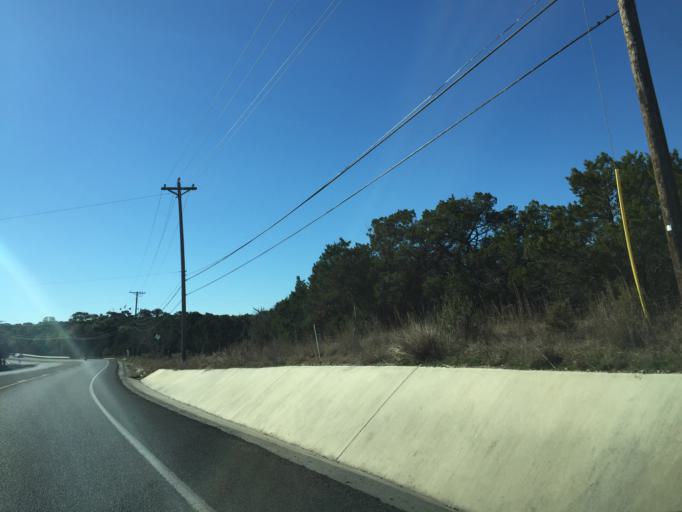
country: US
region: Texas
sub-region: Hays County
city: Woodcreek
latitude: 30.0132
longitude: -98.1210
